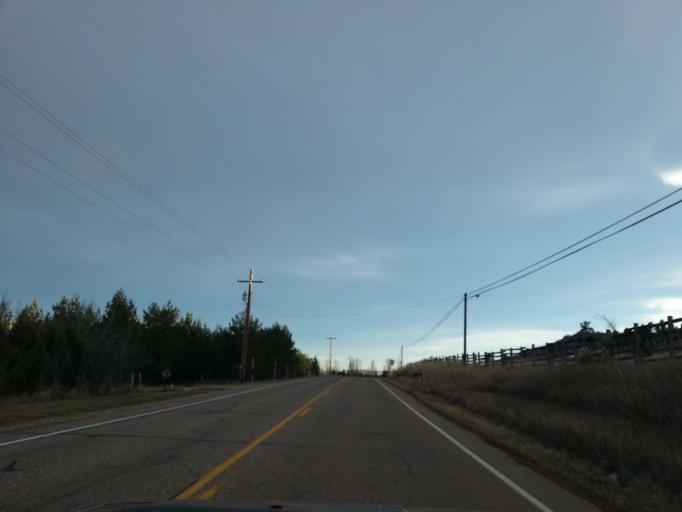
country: US
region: Colorado
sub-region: Larimer County
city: Loveland
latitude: 40.4576
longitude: -105.2064
